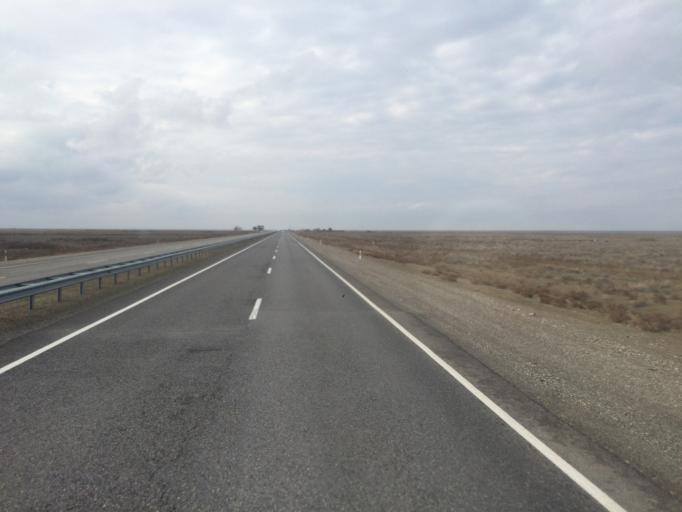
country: KZ
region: Ongtustik Qazaqstan
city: Turkestan
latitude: 43.5230
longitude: 67.7994
